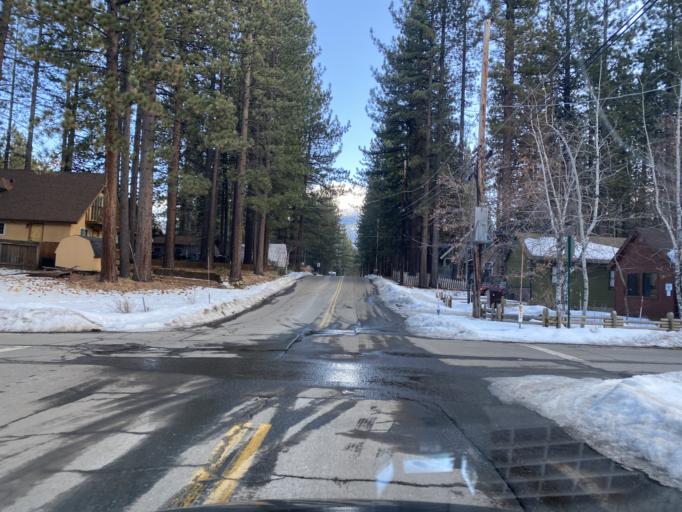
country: US
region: California
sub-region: El Dorado County
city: South Lake Tahoe
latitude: 38.9222
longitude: -119.9784
